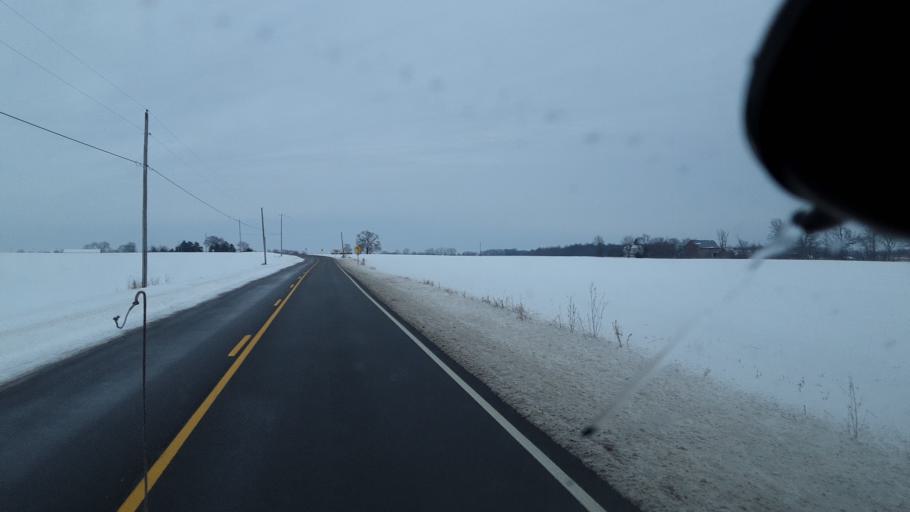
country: US
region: Ohio
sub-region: Union County
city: New California
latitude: 40.2121
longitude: -83.2275
